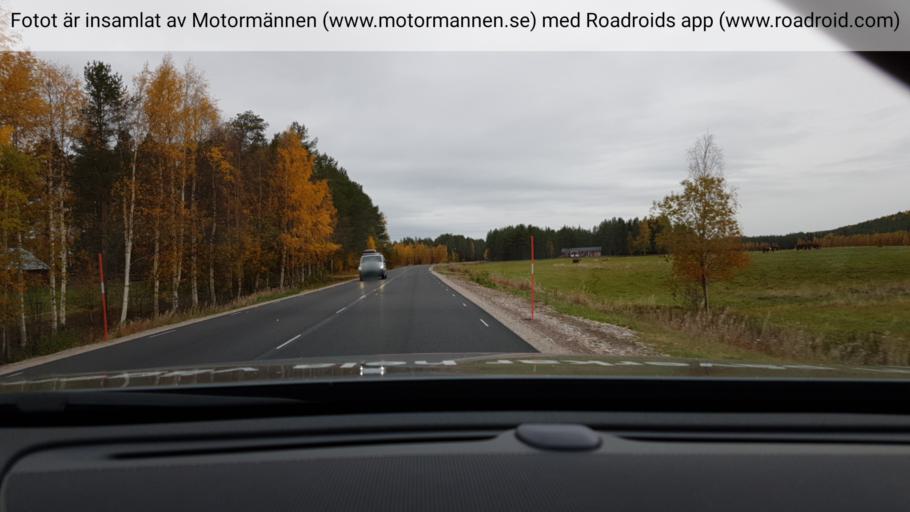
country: SE
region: Norrbotten
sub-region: Overkalix Kommun
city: OEverkalix
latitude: 66.4229
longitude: 22.7999
